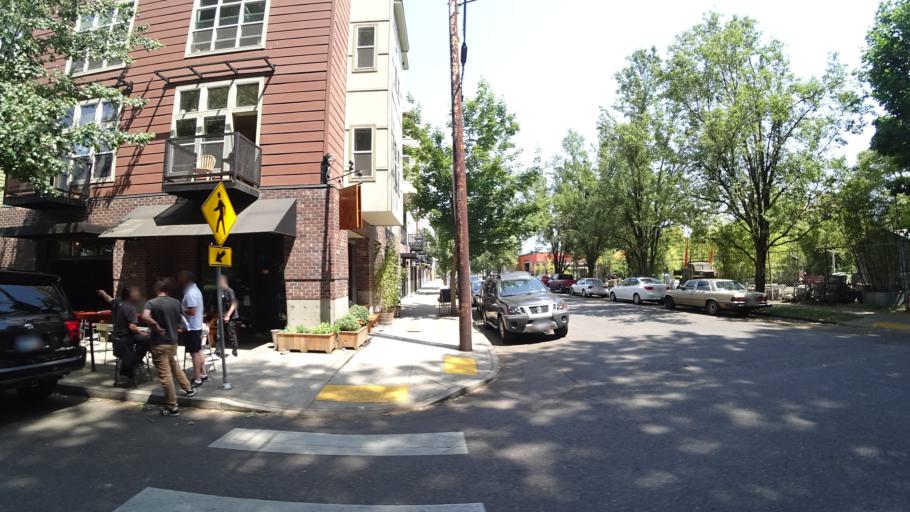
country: US
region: Washington
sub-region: Clark County
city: Vancouver
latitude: 45.5838
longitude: -122.6890
